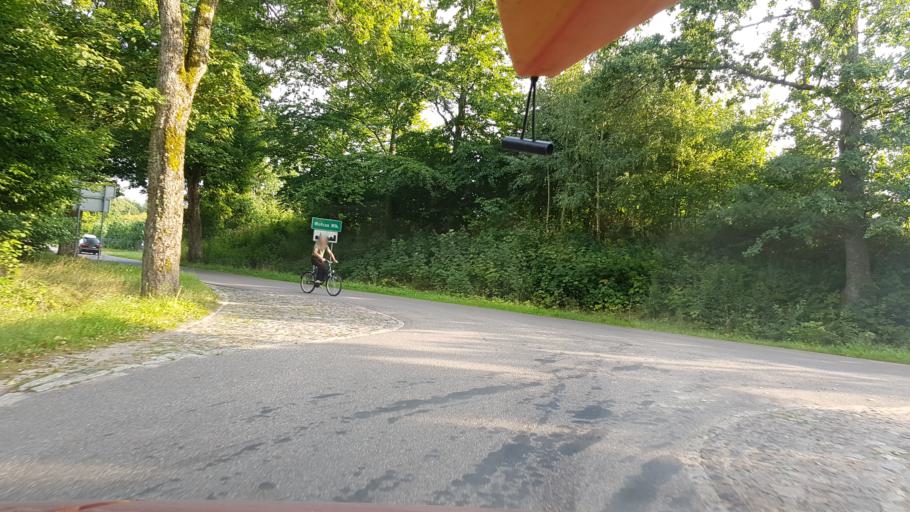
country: PL
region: Pomeranian Voivodeship
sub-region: Powiat bytowski
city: Miastko
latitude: 53.9928
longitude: 16.9191
